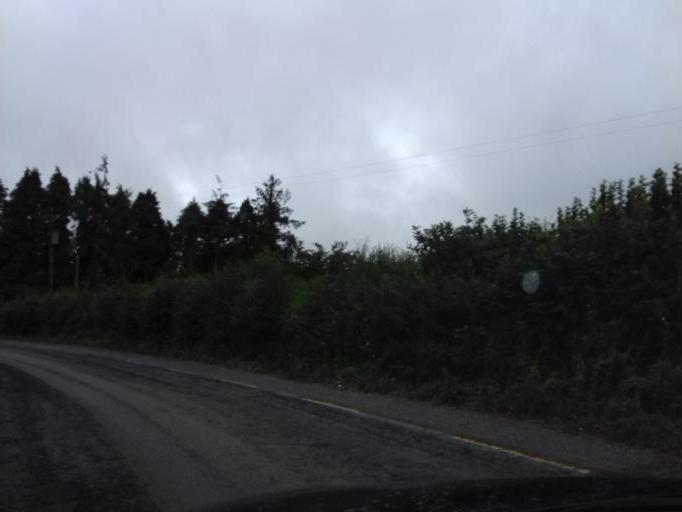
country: IE
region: Leinster
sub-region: County Carlow
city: Bagenalstown
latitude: 52.6192
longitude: -6.9911
